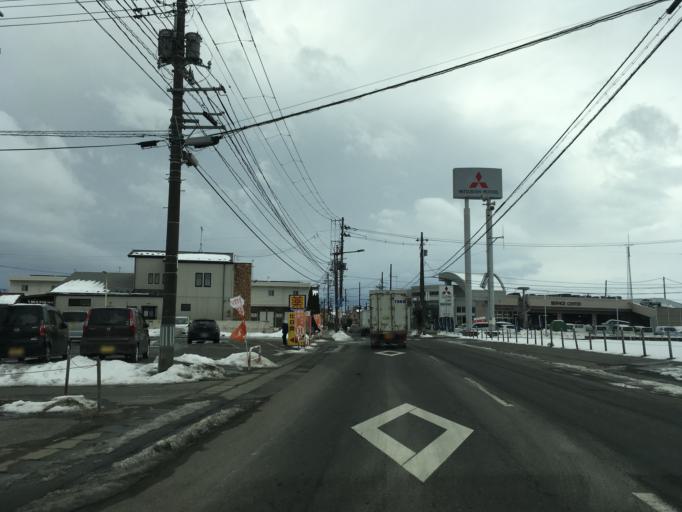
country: JP
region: Miyagi
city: Furukawa
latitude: 38.5811
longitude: 140.9638
